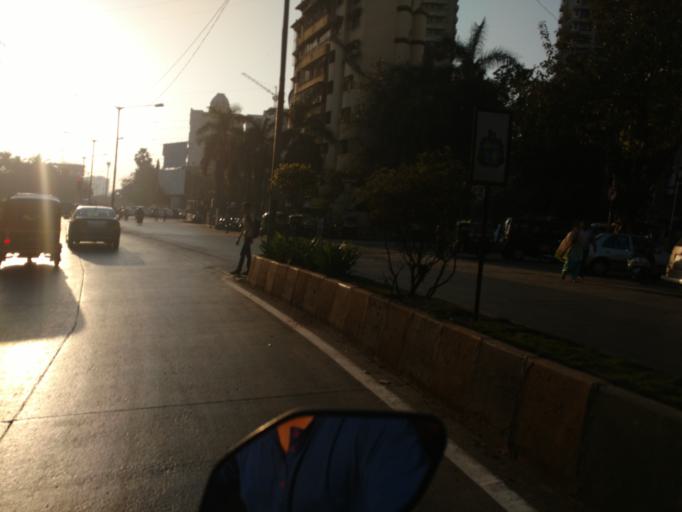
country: IN
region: Maharashtra
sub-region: Mumbai Suburban
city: Borivli
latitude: 19.2076
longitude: 72.8358
